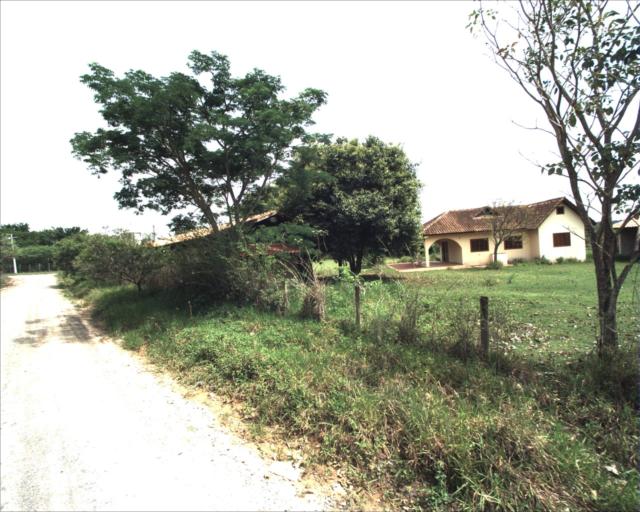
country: BR
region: Sao Paulo
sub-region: Salto De Pirapora
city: Salto de Pirapora
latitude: -23.5666
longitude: -47.5415
